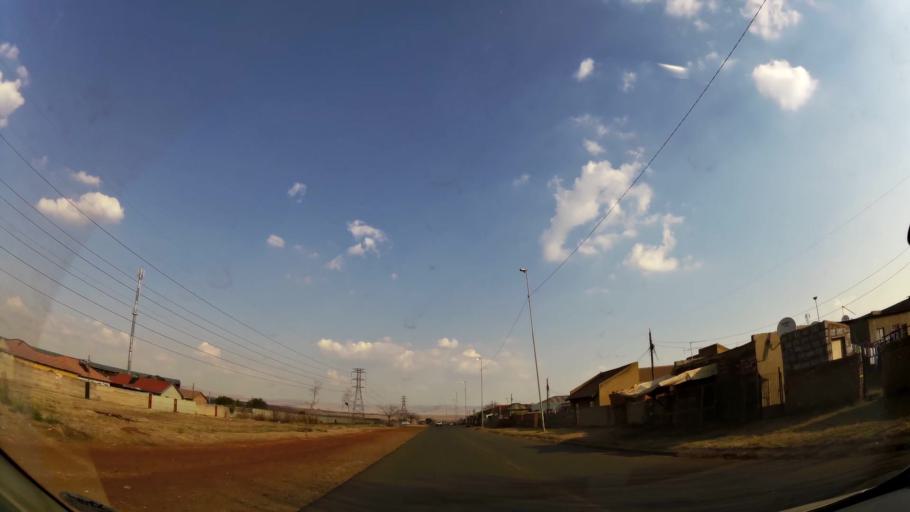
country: ZA
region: Gauteng
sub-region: Ekurhuleni Metropolitan Municipality
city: Germiston
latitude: -26.3609
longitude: 28.2278
